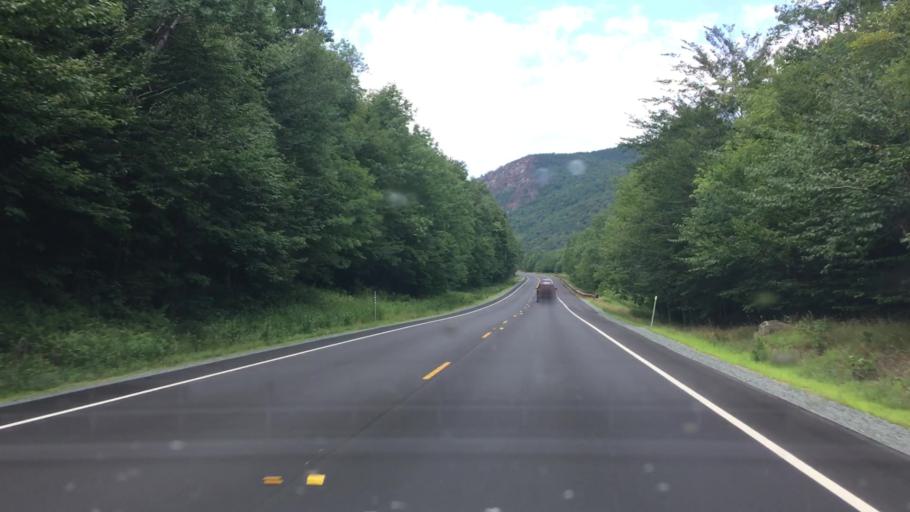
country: US
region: New Hampshire
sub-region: Grafton County
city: Woodstock
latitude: 44.0299
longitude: -71.7642
